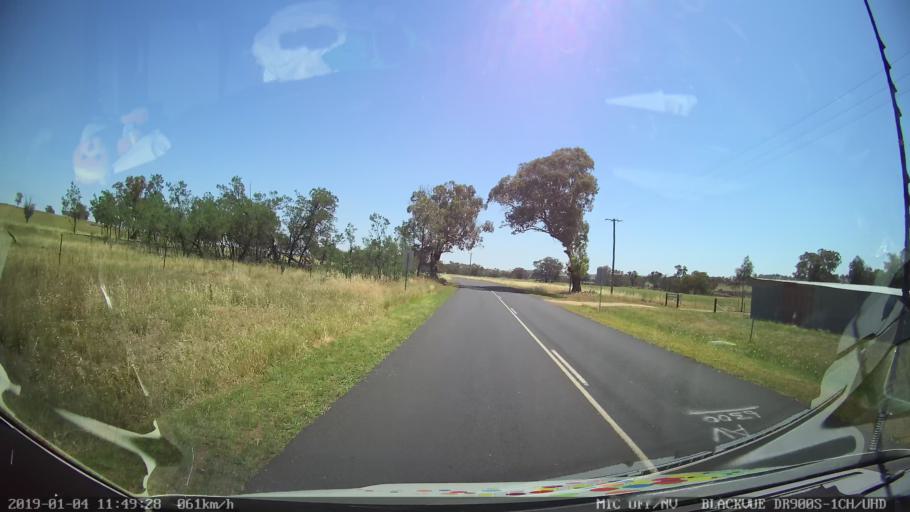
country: AU
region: New South Wales
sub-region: Cabonne
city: Molong
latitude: -32.9183
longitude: 148.7553
